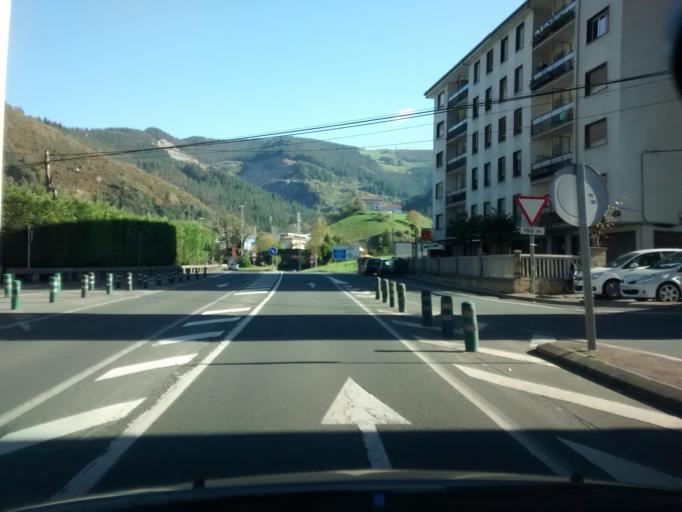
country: ES
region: Basque Country
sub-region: Provincia de Guipuzcoa
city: Elgoibar
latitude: 43.2277
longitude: -2.4032
